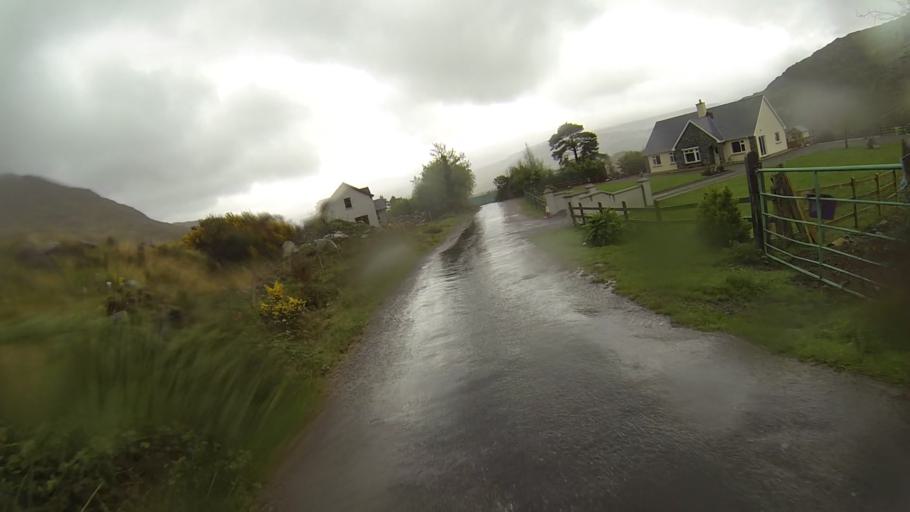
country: IE
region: Munster
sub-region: Ciarrai
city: Kenmare
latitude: 51.9864
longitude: -9.6499
